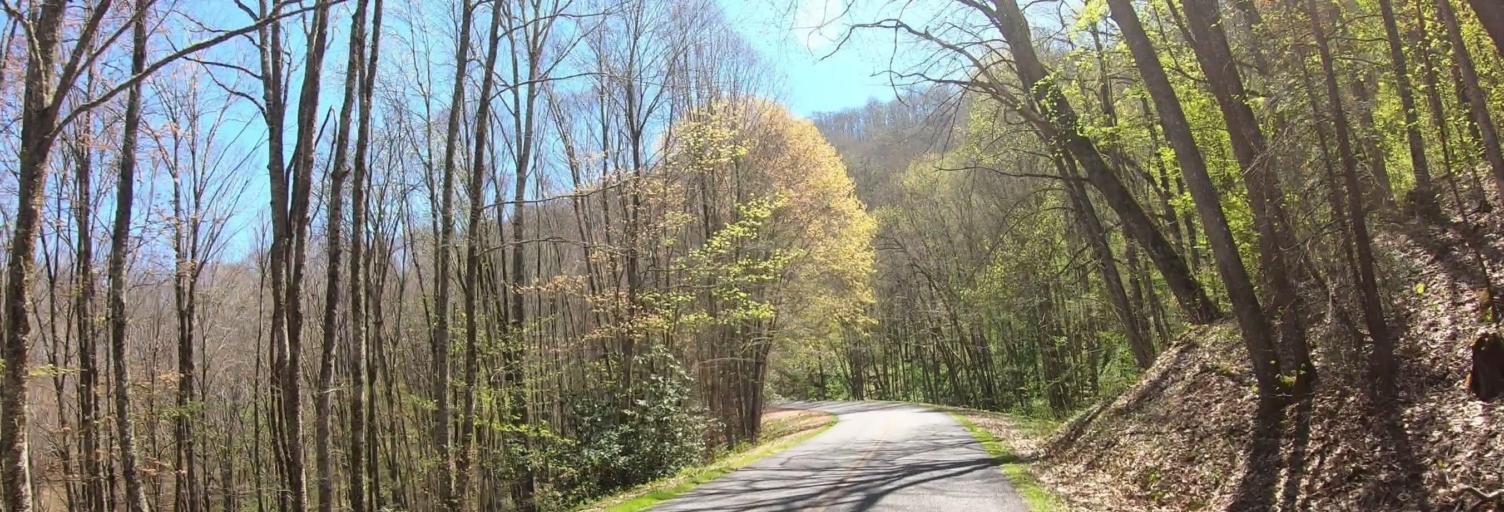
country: US
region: North Carolina
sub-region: Swain County
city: Cherokee
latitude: 35.5265
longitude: -83.2396
